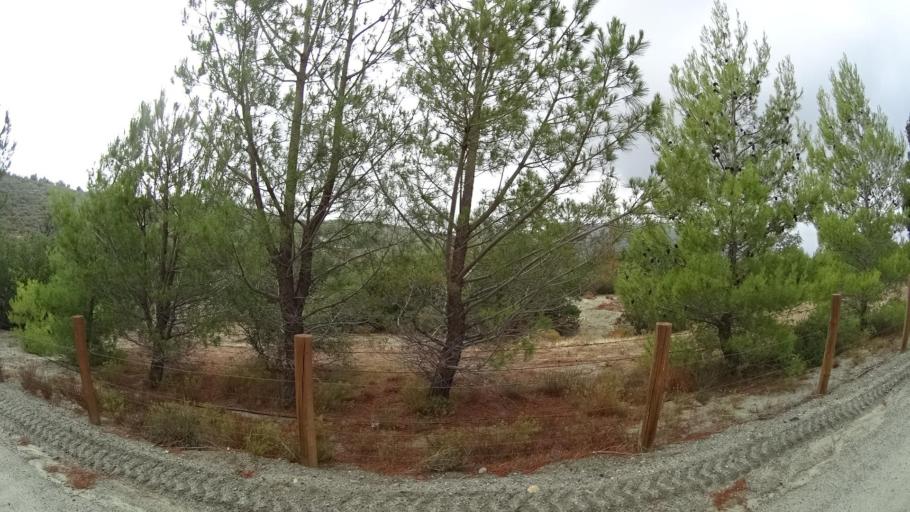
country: US
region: California
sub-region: San Diego County
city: Descanso
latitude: 32.9580
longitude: -116.6439
